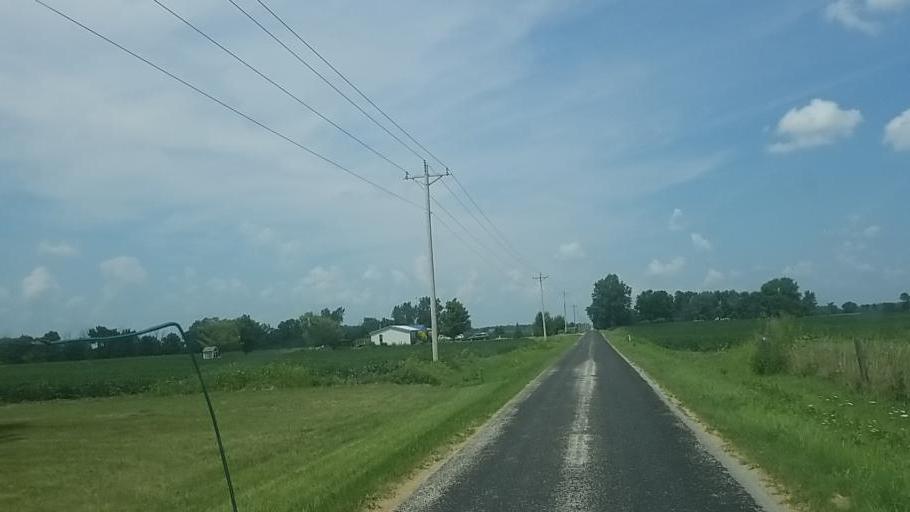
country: US
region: Ohio
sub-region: Union County
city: Richwood
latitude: 40.6289
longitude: -83.3617
